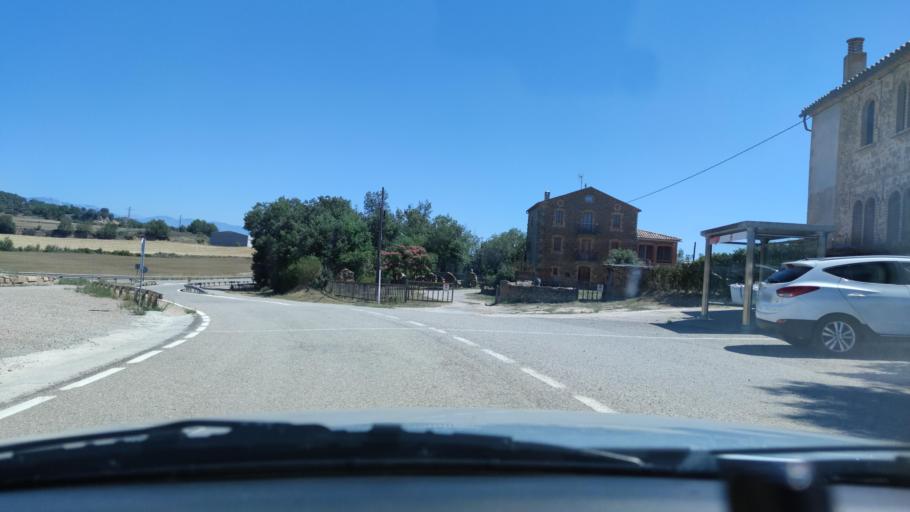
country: ES
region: Catalonia
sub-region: Provincia de Lleida
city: Solsona
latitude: 41.9224
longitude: 1.4629
